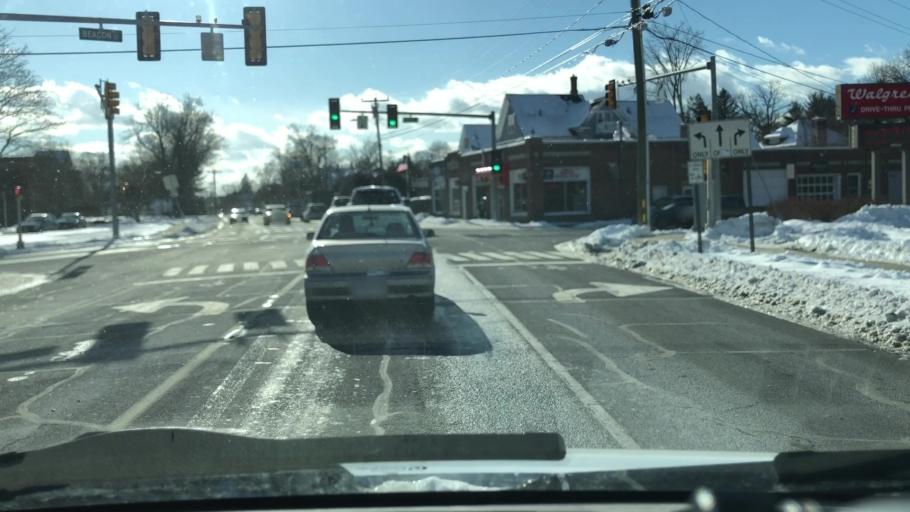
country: US
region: Massachusetts
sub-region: Franklin County
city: Greenfield
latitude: 42.5977
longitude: -72.5967
